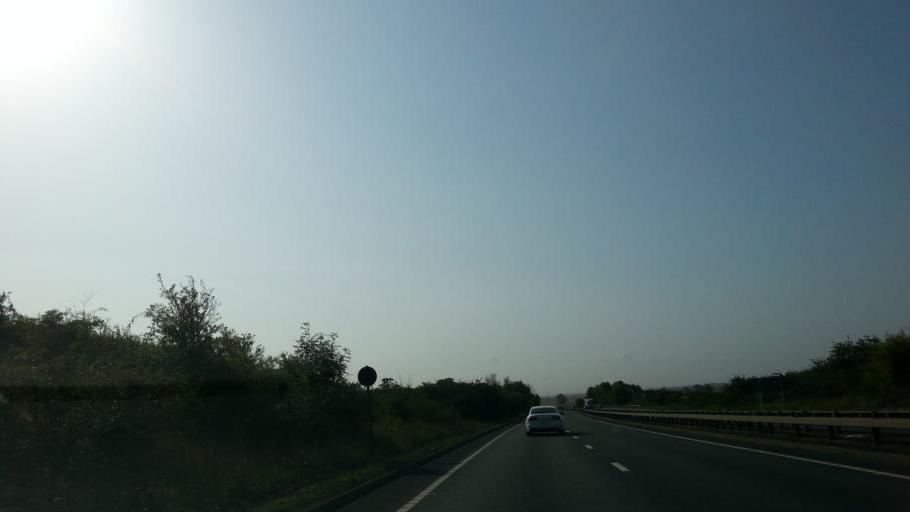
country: GB
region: England
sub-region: Cambridgeshire
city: Great Stukeley
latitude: 52.3658
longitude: -0.2379
